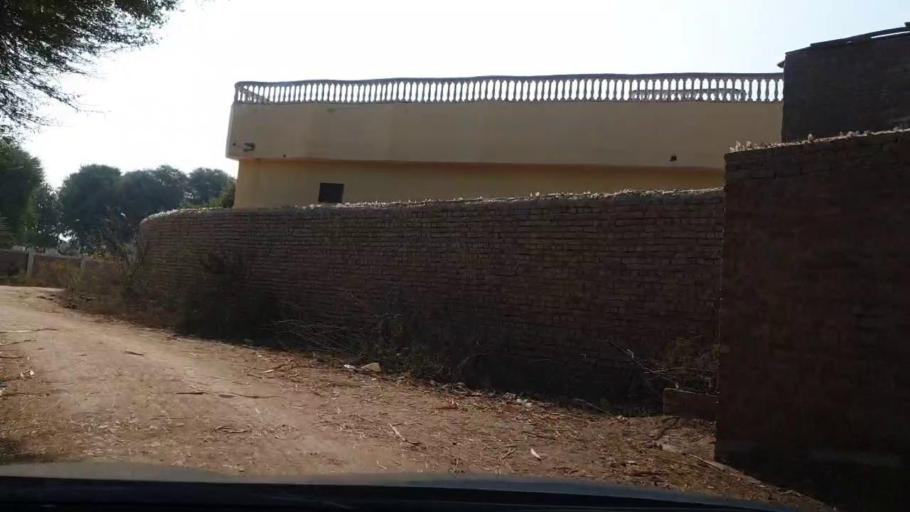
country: PK
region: Sindh
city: Tando Allahyar
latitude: 25.5325
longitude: 68.7685
